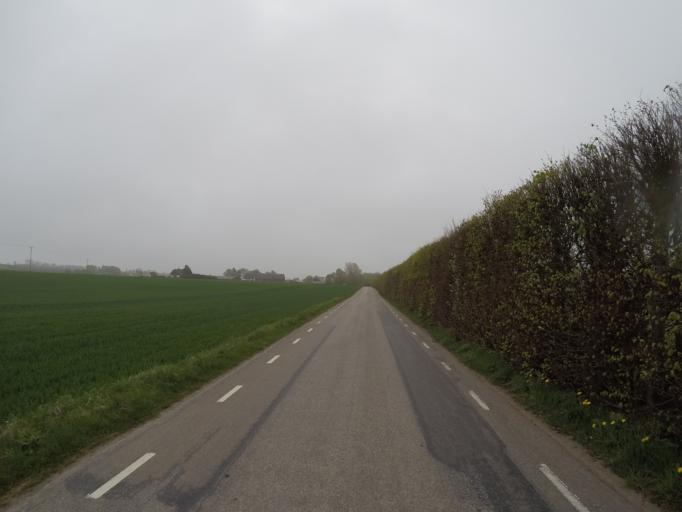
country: SE
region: Halland
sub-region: Laholms Kommun
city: Mellbystrand
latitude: 56.5327
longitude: 12.9772
